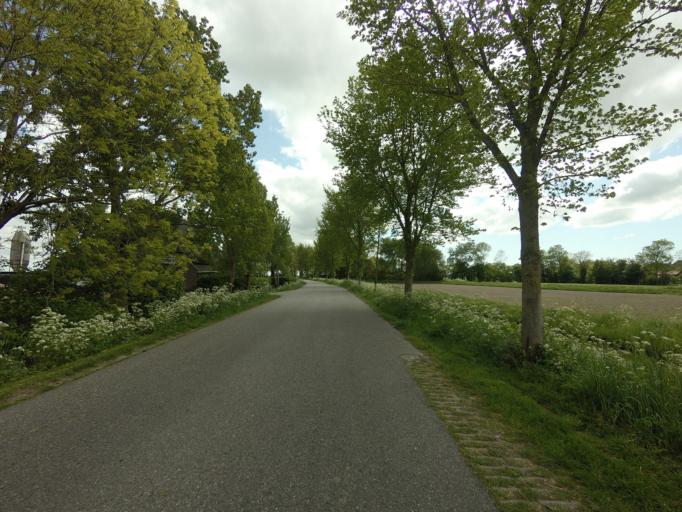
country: NL
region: Friesland
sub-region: Sudwest Fryslan
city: Bolsward
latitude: 53.0856
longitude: 5.5483
